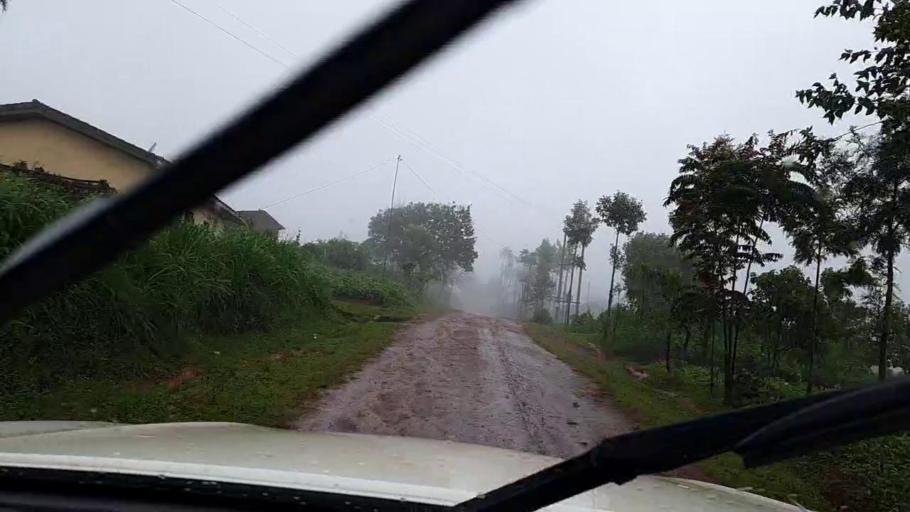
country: RW
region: Northern Province
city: Byumba
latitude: -1.7441
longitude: 30.0045
